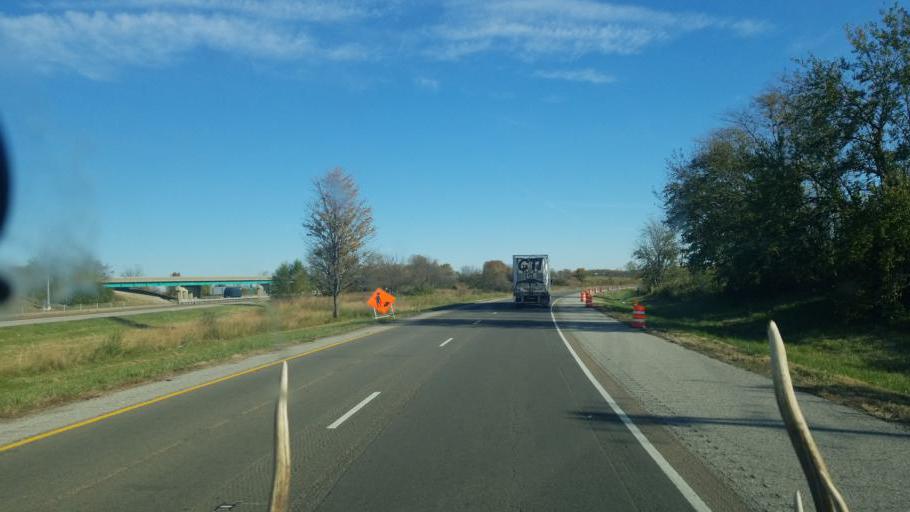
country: US
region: Illinois
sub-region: Madison County
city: Troy
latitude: 38.7465
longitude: -89.9083
